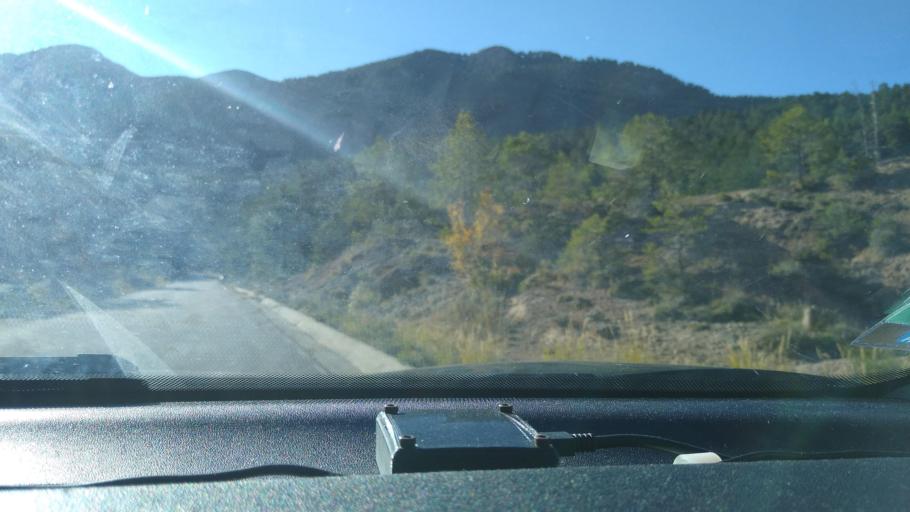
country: ES
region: Catalonia
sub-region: Provincia de Barcelona
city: Saldes
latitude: 42.2125
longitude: 1.7195
